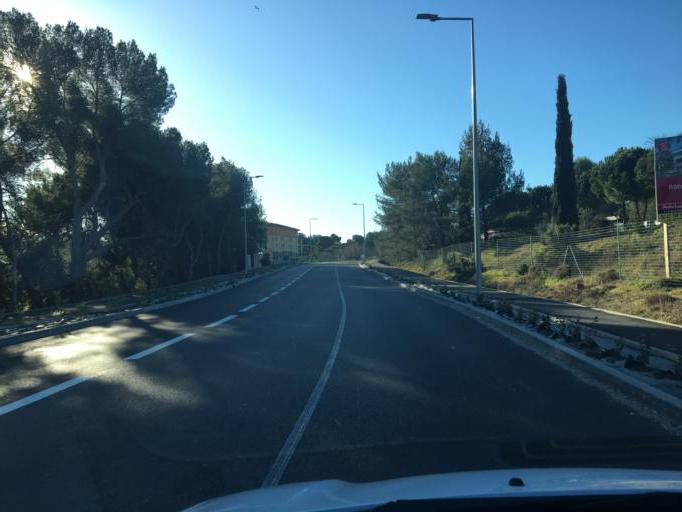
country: FR
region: Provence-Alpes-Cote d'Azur
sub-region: Departement des Bouches-du-Rhone
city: Cabries
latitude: 43.4833
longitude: 5.3642
